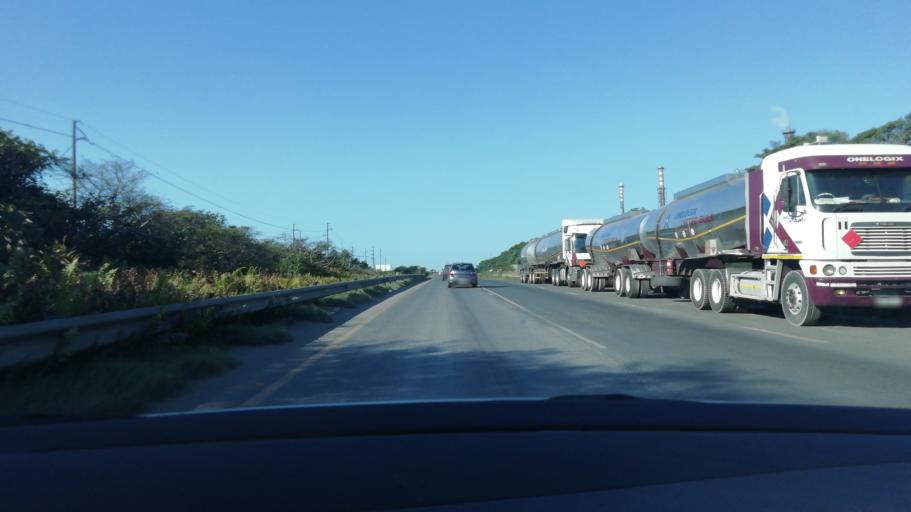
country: ZA
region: KwaZulu-Natal
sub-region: uThungulu District Municipality
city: Richards Bay
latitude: -28.7767
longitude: 32.0309
